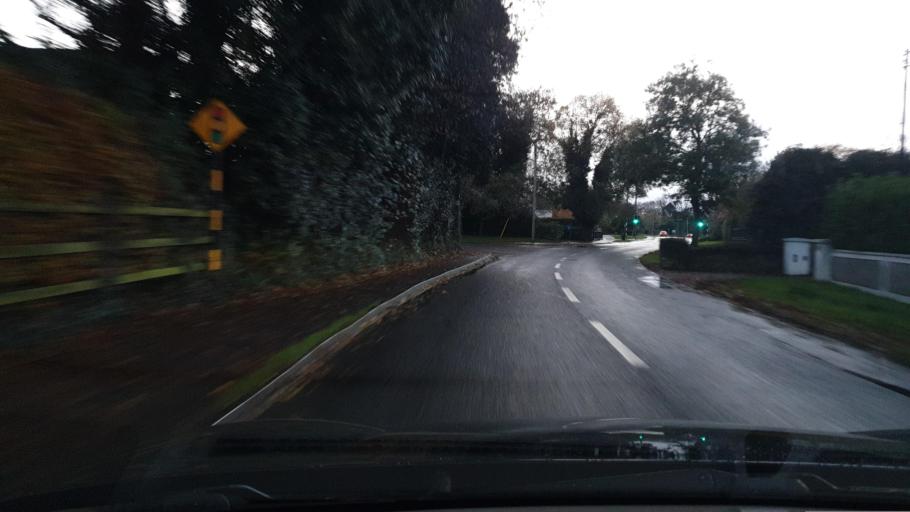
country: IE
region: Leinster
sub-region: Kildare
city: Maynooth
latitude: 53.3751
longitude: -6.6024
